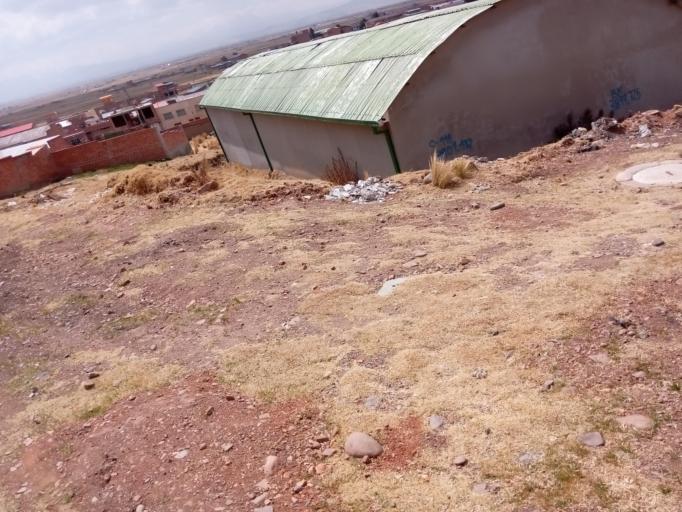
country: BO
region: La Paz
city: Batallas
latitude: -16.3984
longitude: -68.4797
